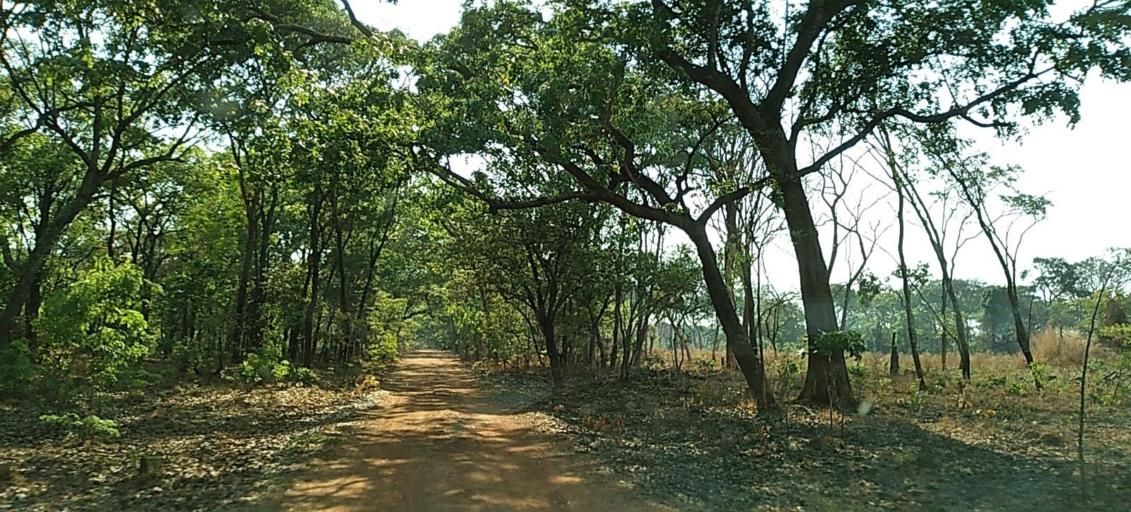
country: ZM
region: Copperbelt
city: Kalulushi
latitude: -13.0054
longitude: 27.7483
